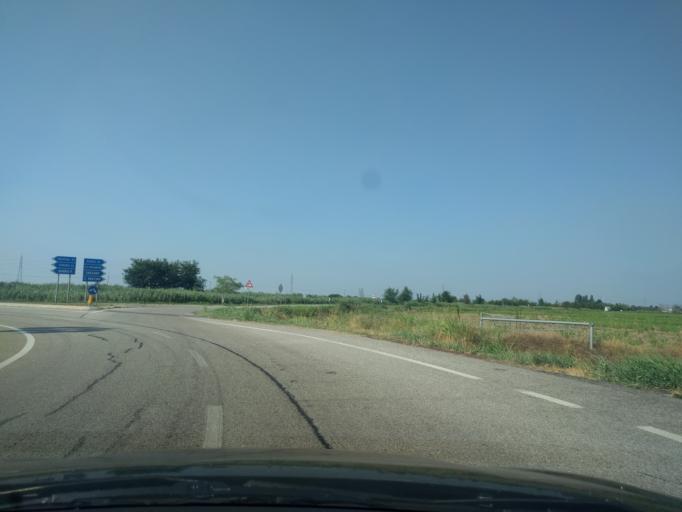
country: IT
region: Veneto
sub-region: Provincia di Rovigo
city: Rovigo
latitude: 45.0866
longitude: 11.8114
